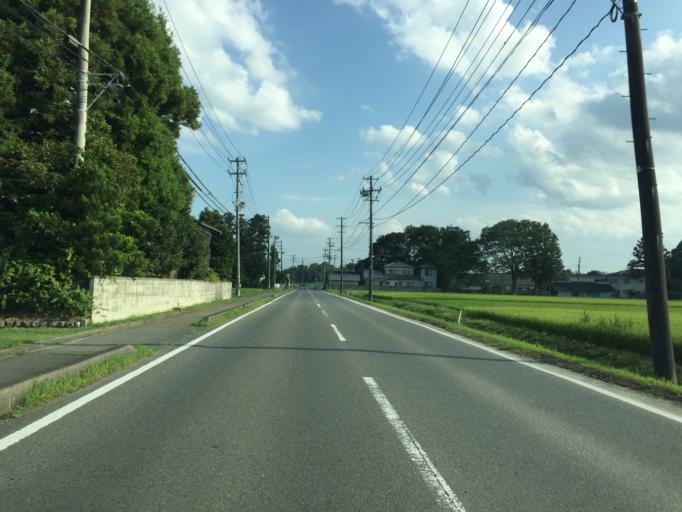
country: JP
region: Miyagi
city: Marumori
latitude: 37.7840
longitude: 140.9144
